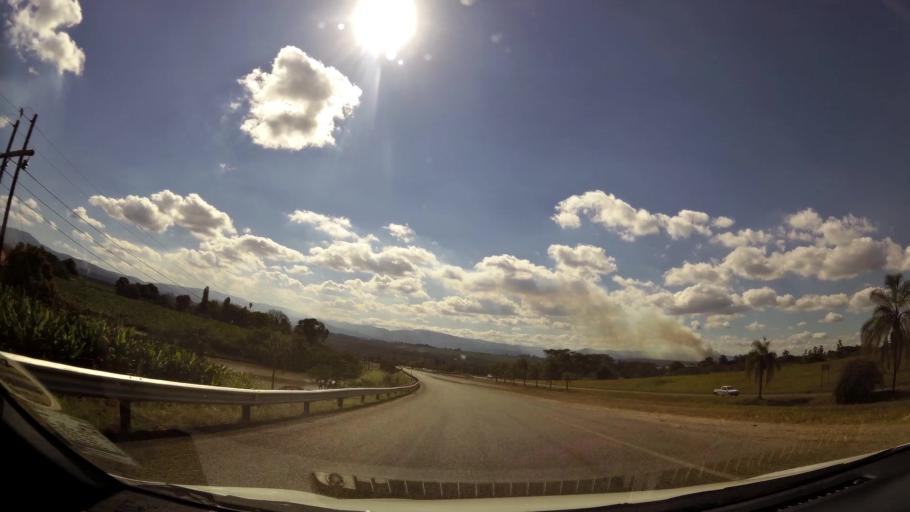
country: ZA
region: Limpopo
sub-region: Mopani District Municipality
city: Tzaneen
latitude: -23.8345
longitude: 30.1355
